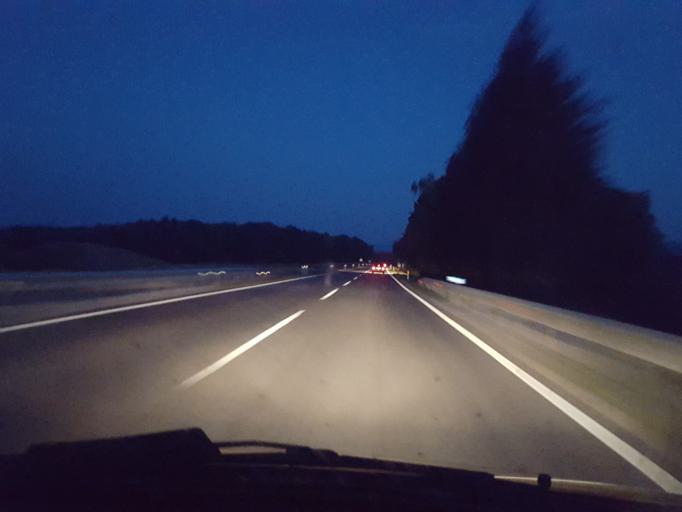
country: AT
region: Lower Austria
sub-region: Politischer Bezirk Scheibbs
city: Purgstall
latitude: 48.0940
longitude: 15.1345
